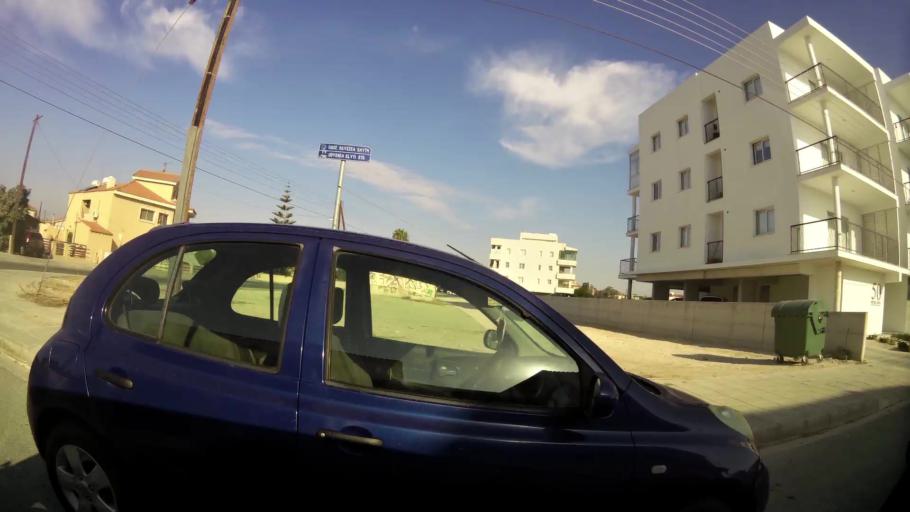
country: CY
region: Larnaka
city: Aradippou
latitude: 34.9378
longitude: 33.5974
